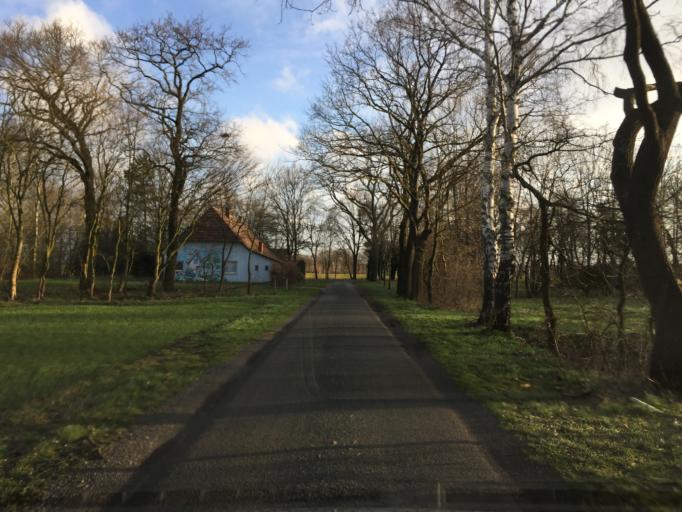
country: DE
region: Lower Saxony
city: Borstel
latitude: 52.6127
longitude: 8.9168
